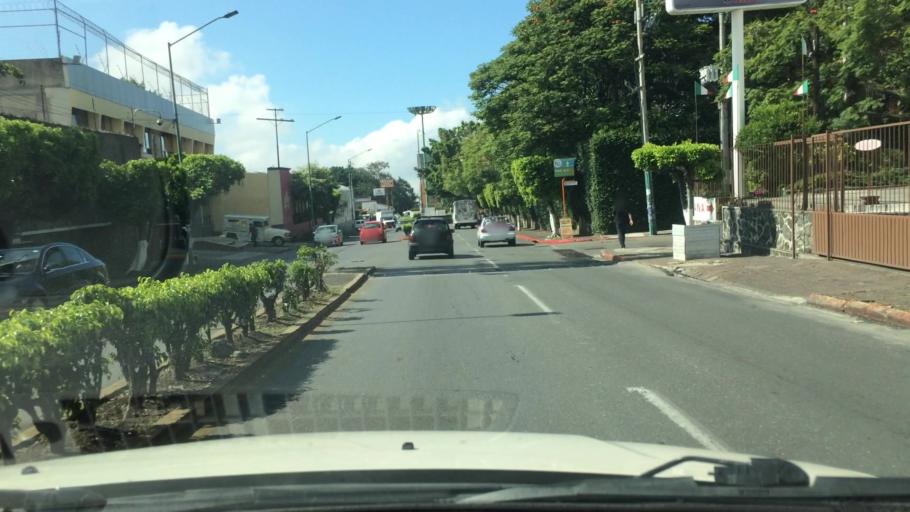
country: MX
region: Morelos
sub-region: Cuernavaca
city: Fraccionamiento Lomas de Ahuatlan
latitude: 18.9516
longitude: -99.2449
